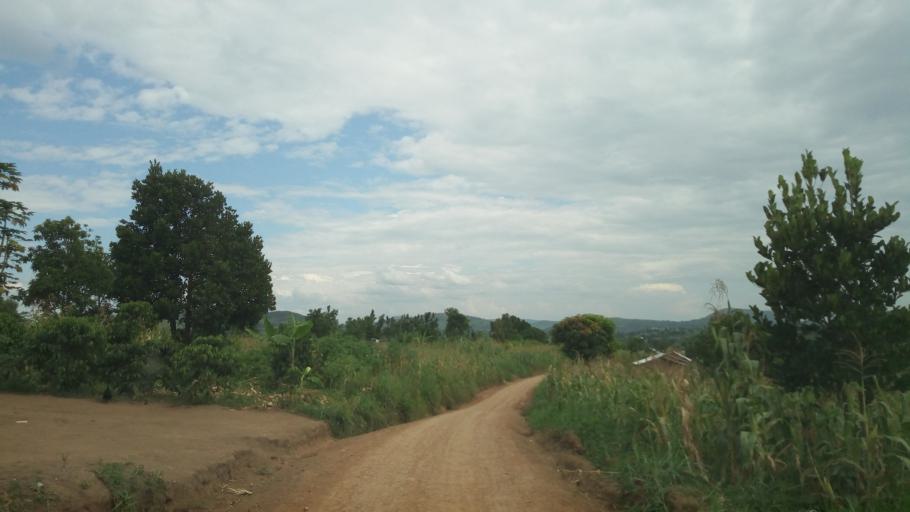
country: UG
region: Central Region
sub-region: Kiboga District
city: Kiboga
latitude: 0.7633
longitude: 31.6868
